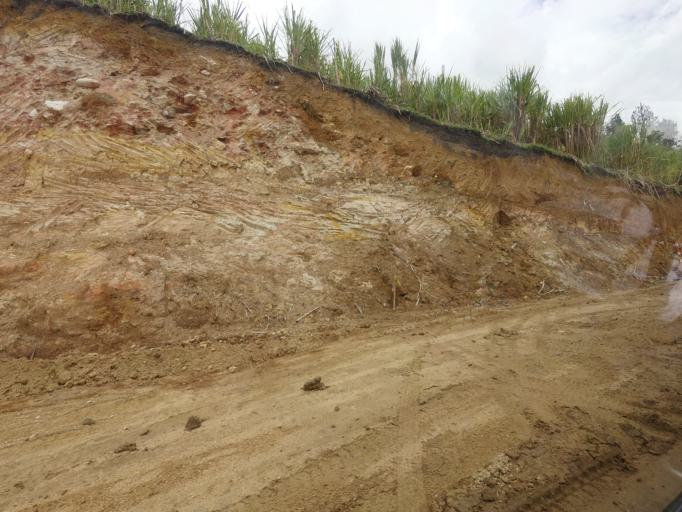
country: CO
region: Huila
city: San Agustin
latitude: 1.9569
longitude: -76.2974
